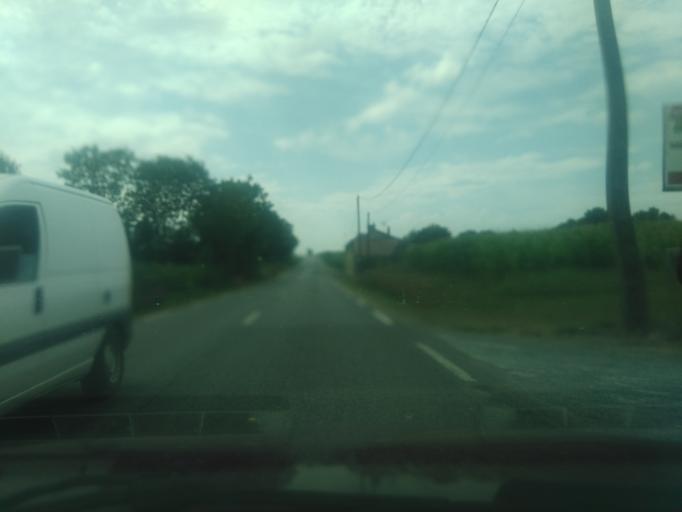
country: FR
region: Pays de la Loire
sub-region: Departement de la Vendee
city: La Tardiere
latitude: 46.6521
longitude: -0.6914
